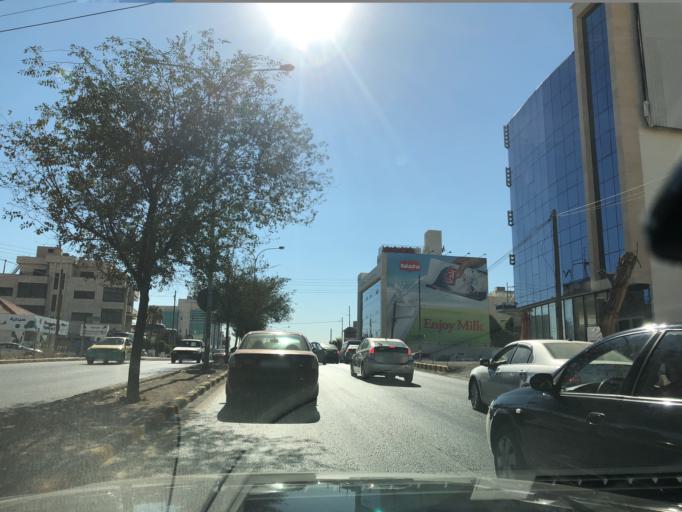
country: JO
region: Amman
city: Al Jubayhah
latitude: 31.9726
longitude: 35.8738
